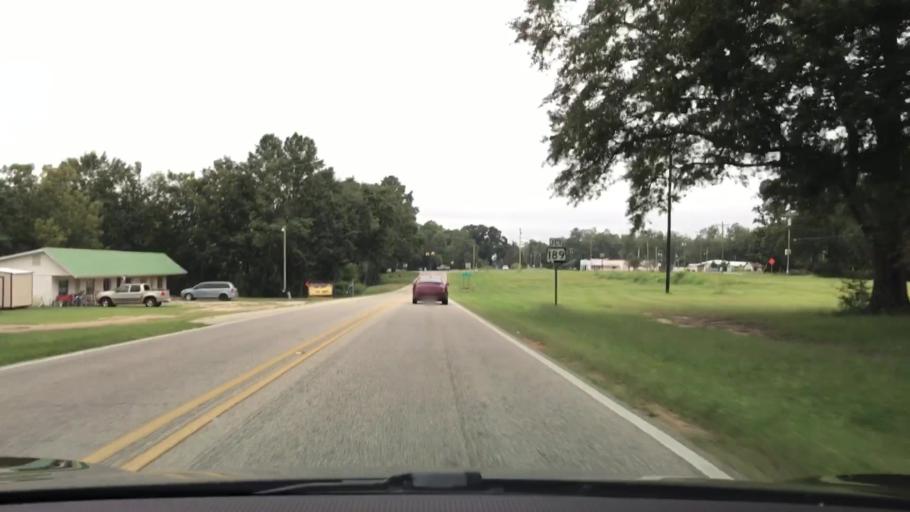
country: US
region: Alabama
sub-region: Covington County
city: Opp
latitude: 31.2136
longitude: -86.1693
